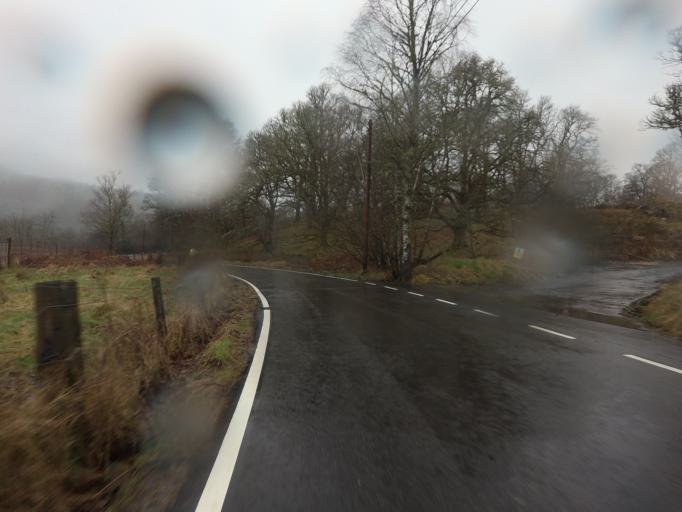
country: GB
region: Scotland
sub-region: Stirling
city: Killearn
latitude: 56.1917
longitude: -4.5075
